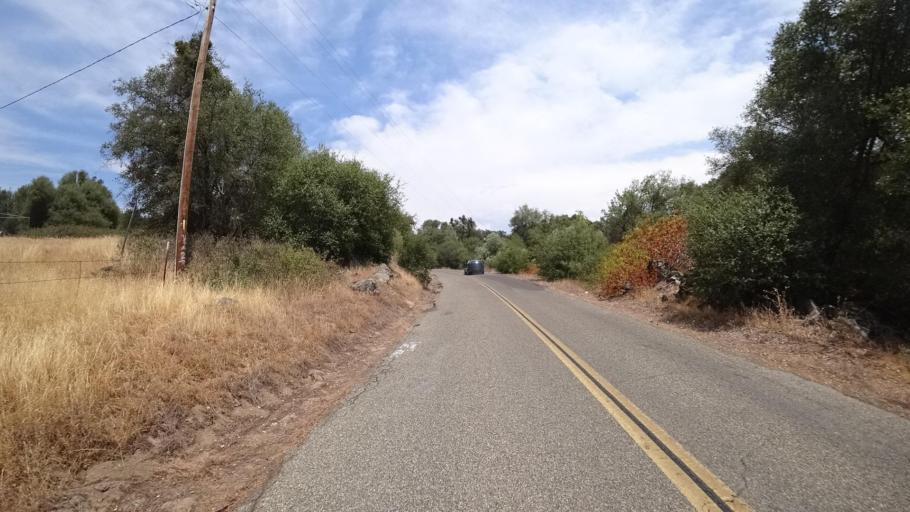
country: US
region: California
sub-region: Mariposa County
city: Mariposa
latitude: 37.4247
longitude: -119.8600
